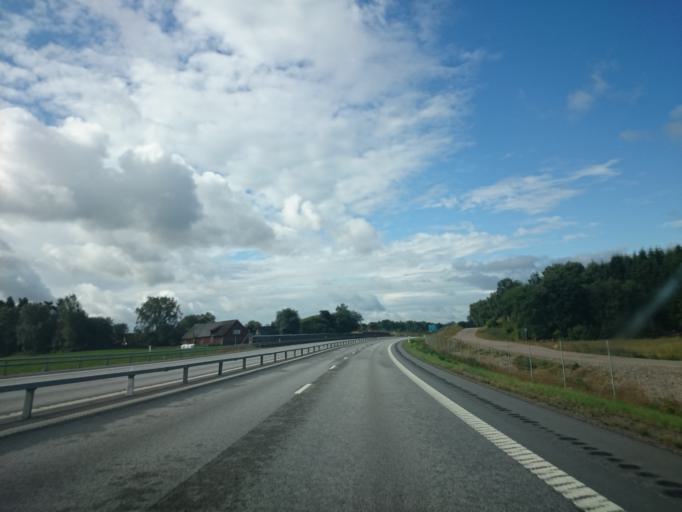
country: SE
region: Skane
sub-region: Horby Kommun
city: Hoerby
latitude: 55.8770
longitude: 13.7107
